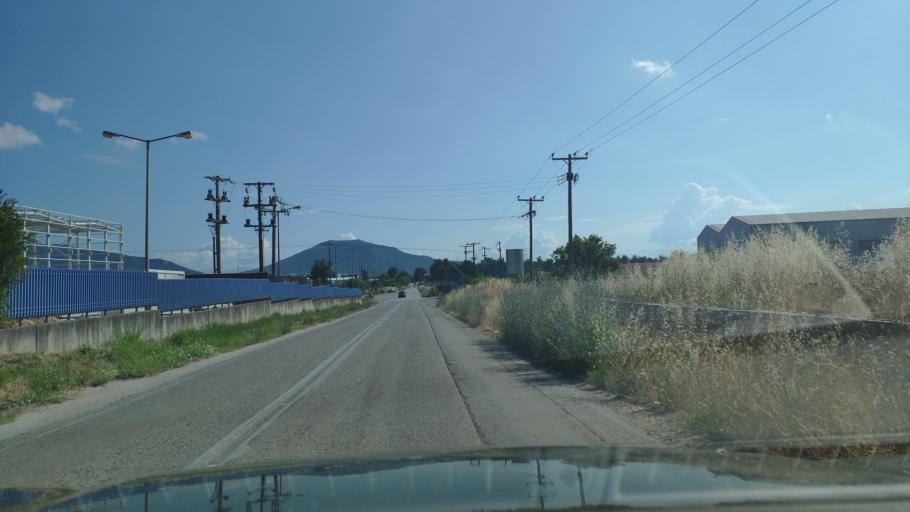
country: GR
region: Central Greece
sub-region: Nomos Voiotias
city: Arma
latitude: 38.3843
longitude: 23.4990
